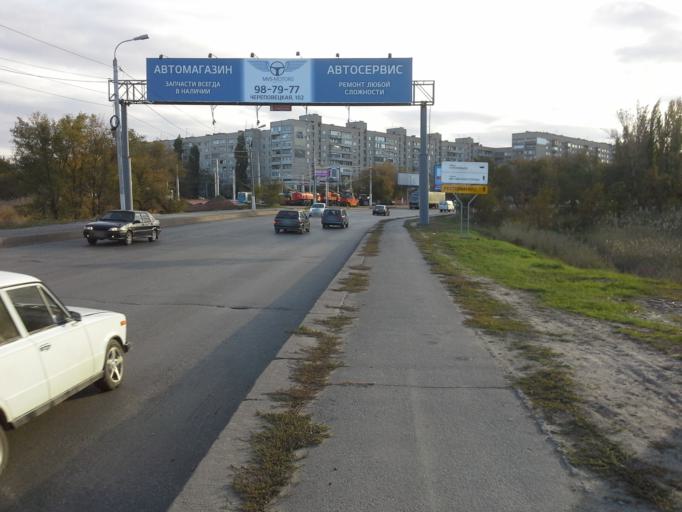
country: RU
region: Volgograd
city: Vodstroy
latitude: 48.8250
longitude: 44.6419
